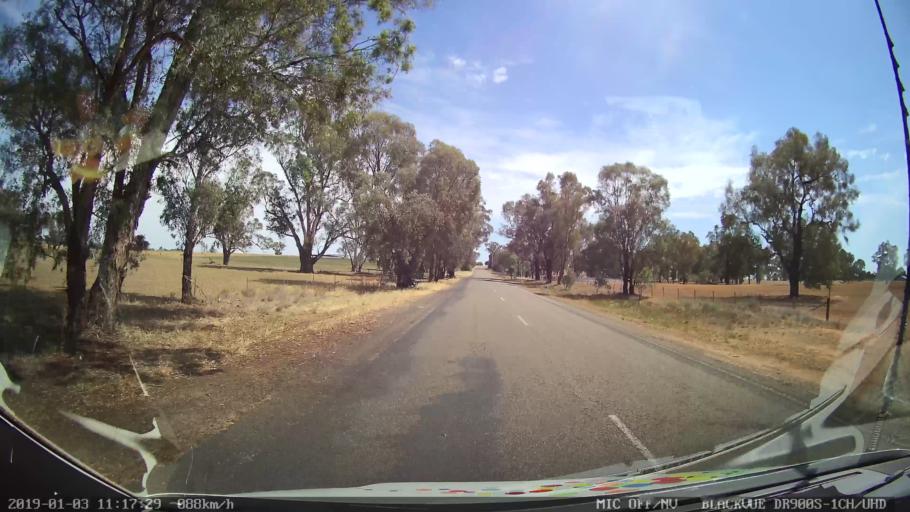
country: AU
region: New South Wales
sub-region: Young
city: Young
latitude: -34.1380
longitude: 148.2657
